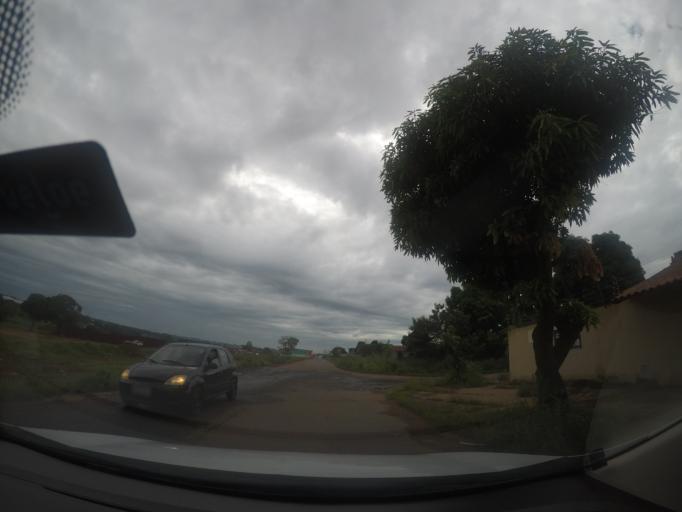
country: BR
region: Goias
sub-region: Goiania
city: Goiania
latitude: -16.6423
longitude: -49.3343
